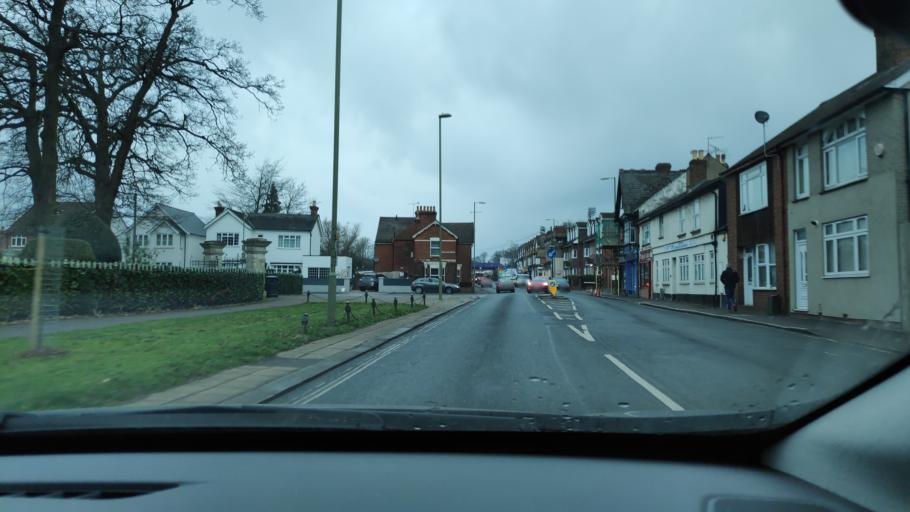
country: GB
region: England
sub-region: Hampshire
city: Aldershot
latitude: 51.2454
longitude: -0.7547
